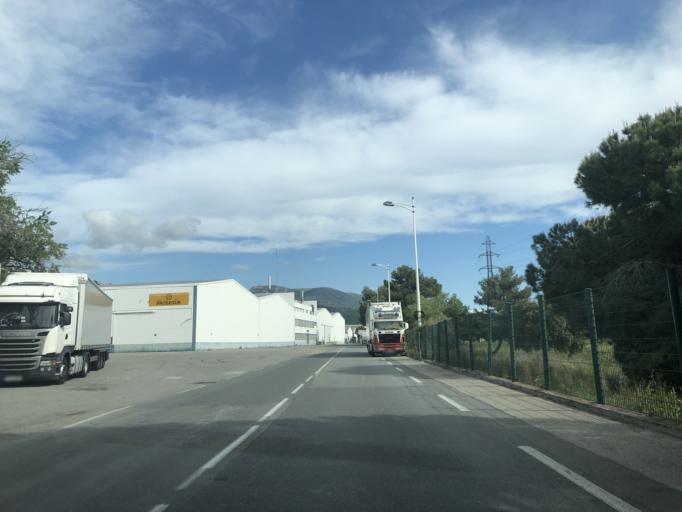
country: FR
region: Provence-Alpes-Cote d'Azur
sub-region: Departement des Alpes-Maritimes
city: Saint-Laurent-du-Var
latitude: 43.6927
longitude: 7.1853
